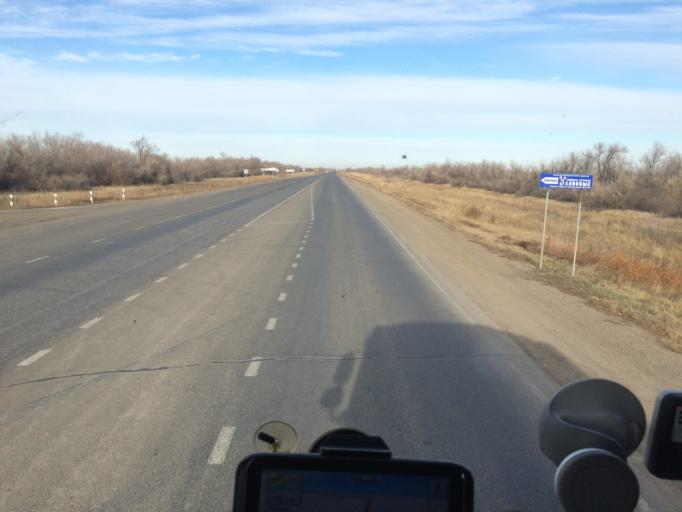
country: KZ
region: Batys Qazaqstan
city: Oral
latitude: 51.3116
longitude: 51.3510
